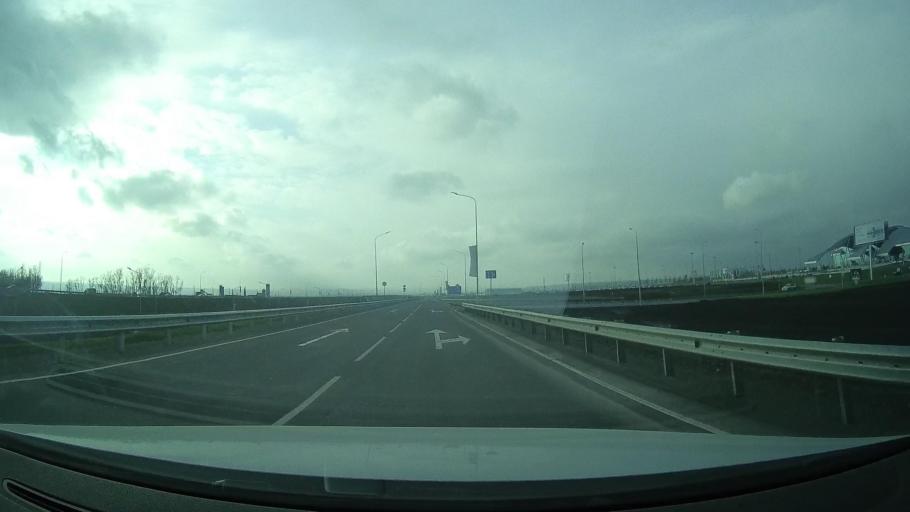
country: RU
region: Rostov
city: Grushevskaya
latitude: 47.4866
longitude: 39.9352
